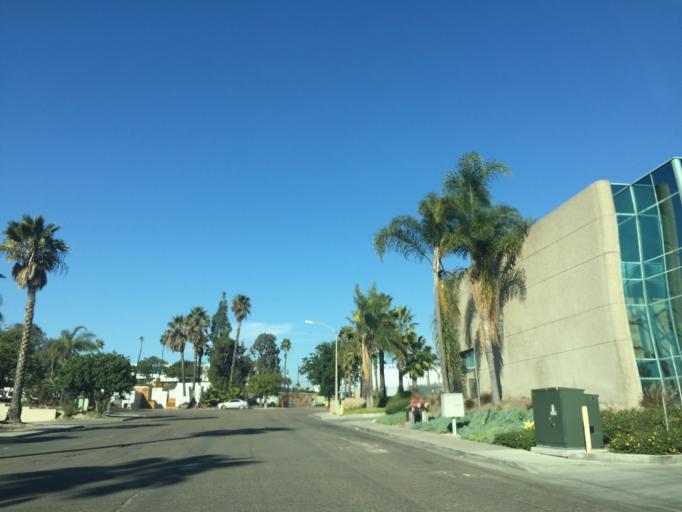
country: MX
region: Baja California
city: Tijuana
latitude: 32.5552
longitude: -116.9340
